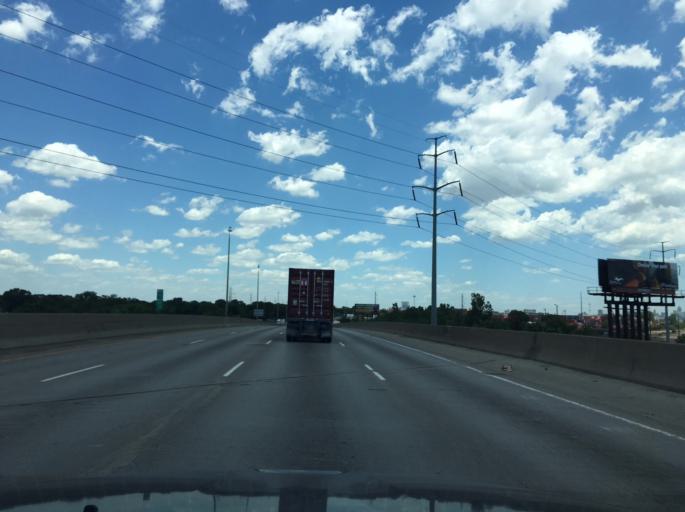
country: US
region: Michigan
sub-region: Wayne County
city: River Rouge
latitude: 42.2934
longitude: -83.1276
